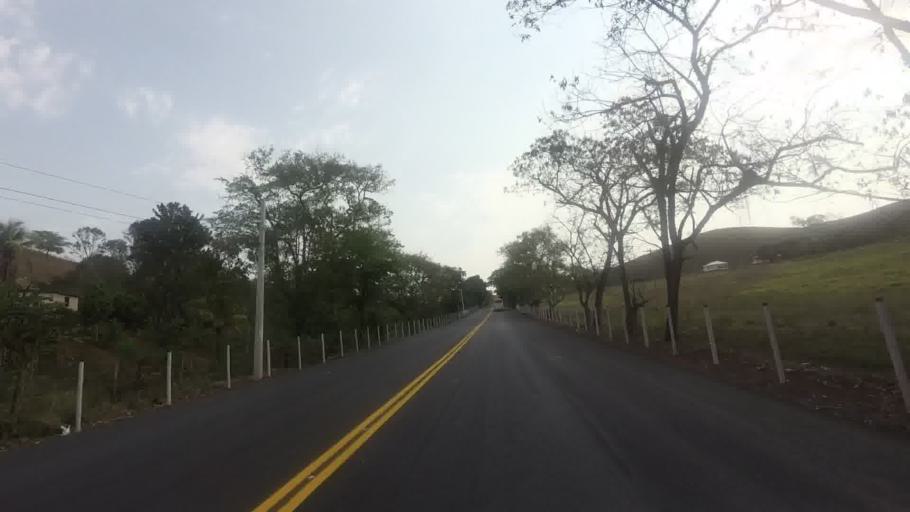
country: BR
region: Rio de Janeiro
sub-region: Itaperuna
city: Itaperuna
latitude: -21.2502
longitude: -41.7613
